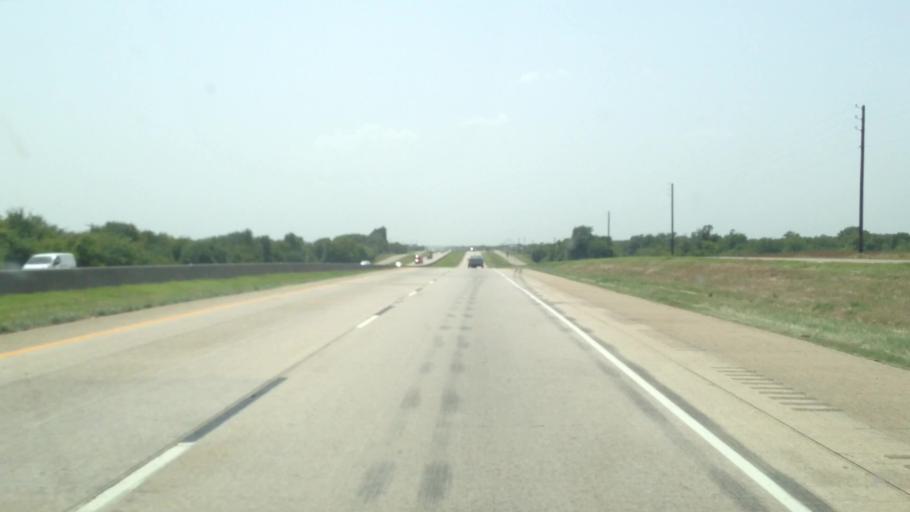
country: US
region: Texas
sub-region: Hopkins County
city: Sulphur Springs
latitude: 33.1211
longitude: -95.6562
